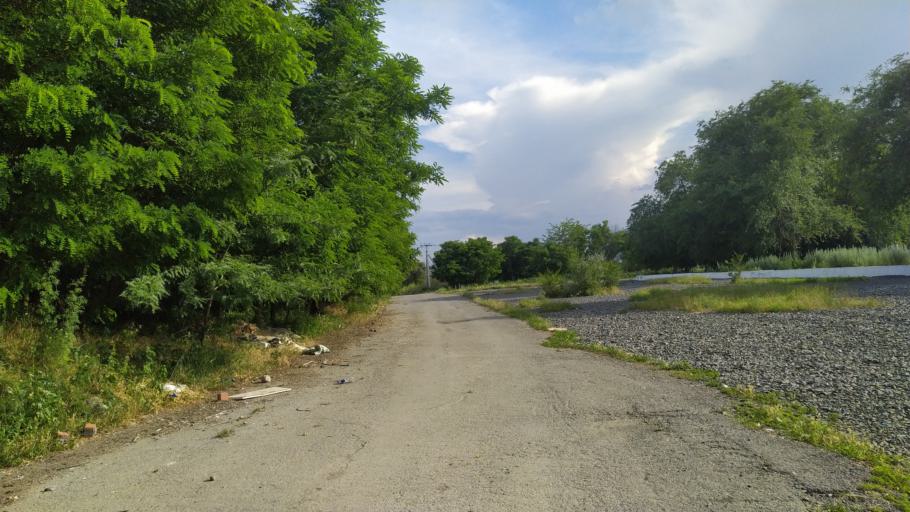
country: RU
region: Rostov
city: Bataysk
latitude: 47.1176
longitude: 39.7118
